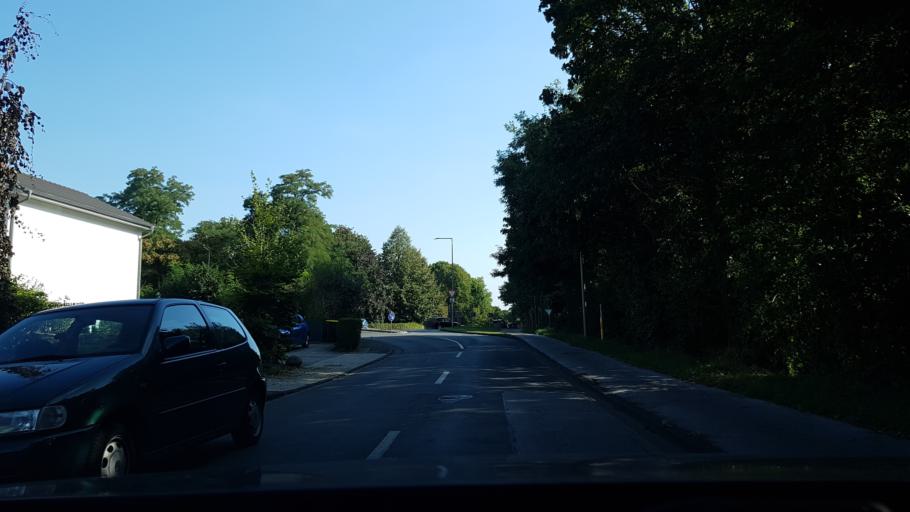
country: DE
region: North Rhine-Westphalia
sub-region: Regierungsbezirk Dusseldorf
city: Duisburg
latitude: 51.3993
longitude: 6.7964
